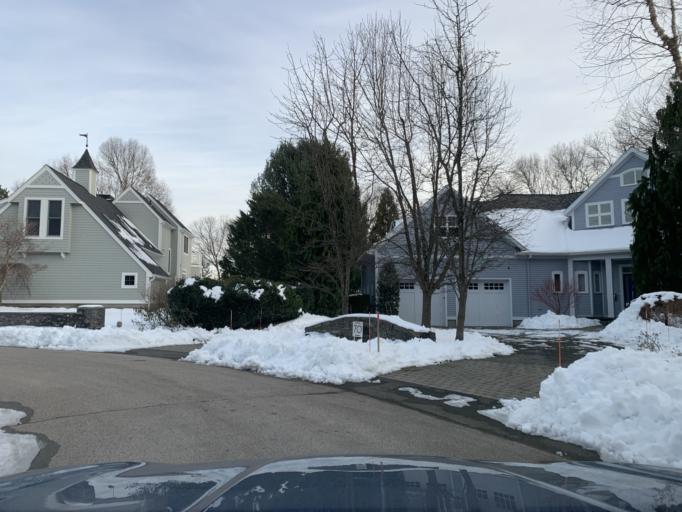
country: US
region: Rhode Island
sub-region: Washington County
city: North Kingstown
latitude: 41.5825
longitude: -71.4483
